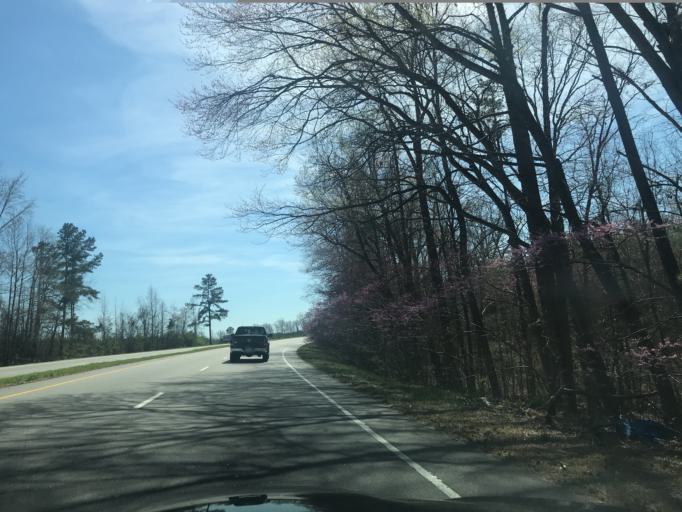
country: US
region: North Carolina
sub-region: Wake County
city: Garner
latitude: 35.6787
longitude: -78.6868
